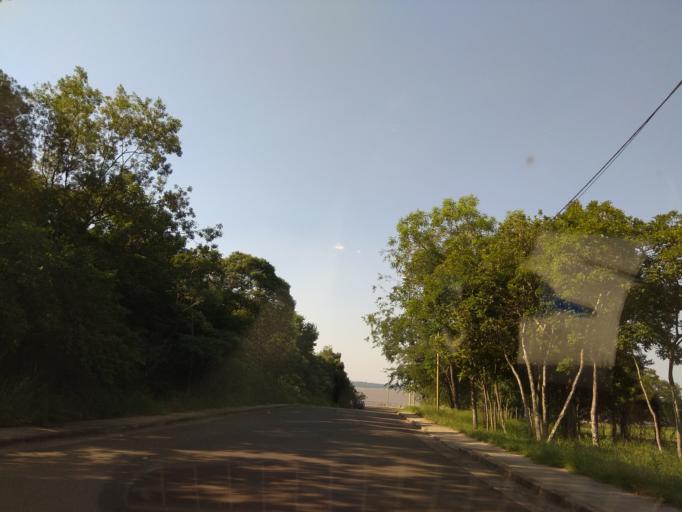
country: AR
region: Misiones
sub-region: Departamento de Capital
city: Posadas
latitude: -27.3545
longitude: -55.9414
